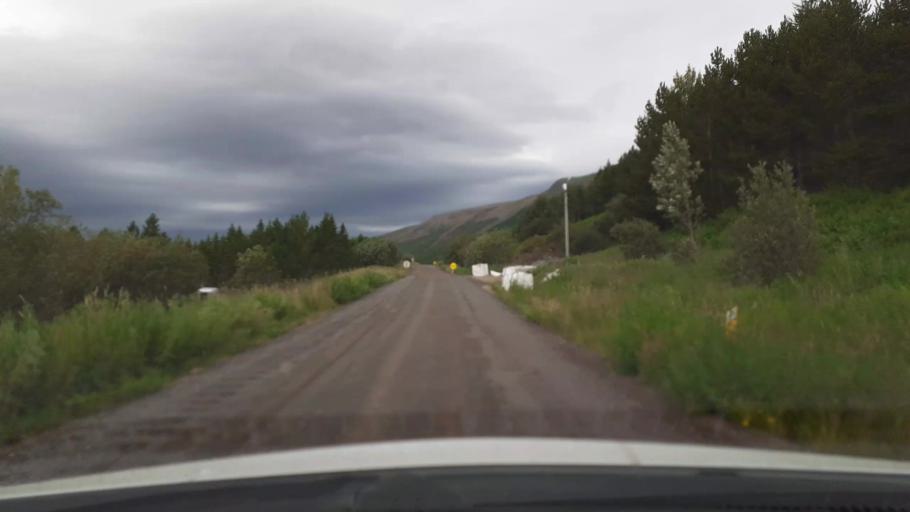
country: IS
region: West
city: Borgarnes
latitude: 64.5309
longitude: -21.5119
